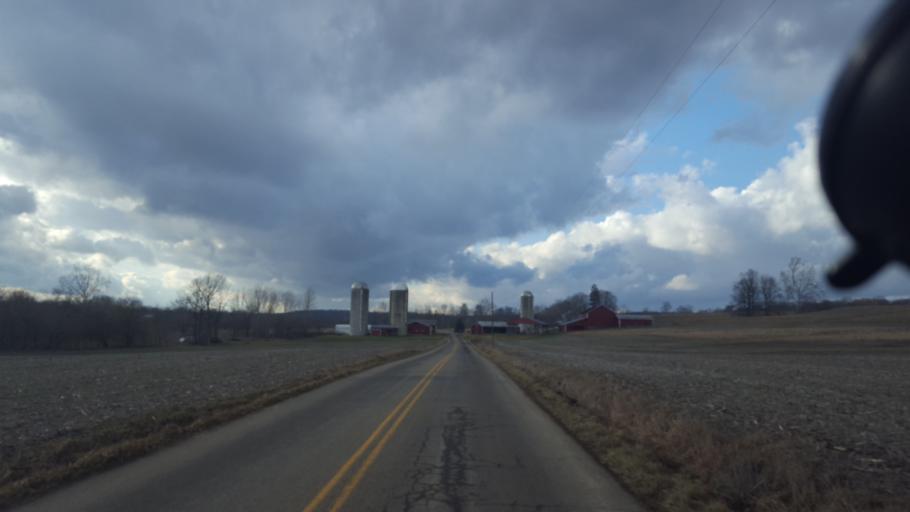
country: US
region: Ohio
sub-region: Knox County
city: Fredericktown
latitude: 40.5426
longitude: -82.6056
